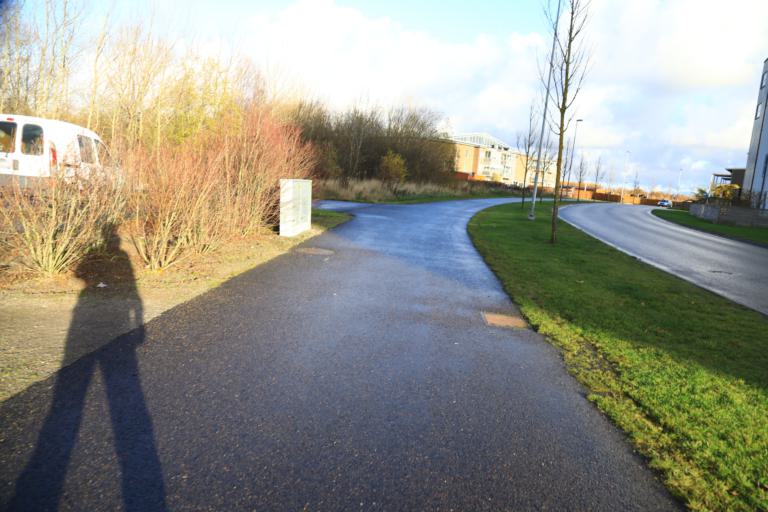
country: SE
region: Halland
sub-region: Varbergs Kommun
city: Traslovslage
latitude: 57.0881
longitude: 12.2777
